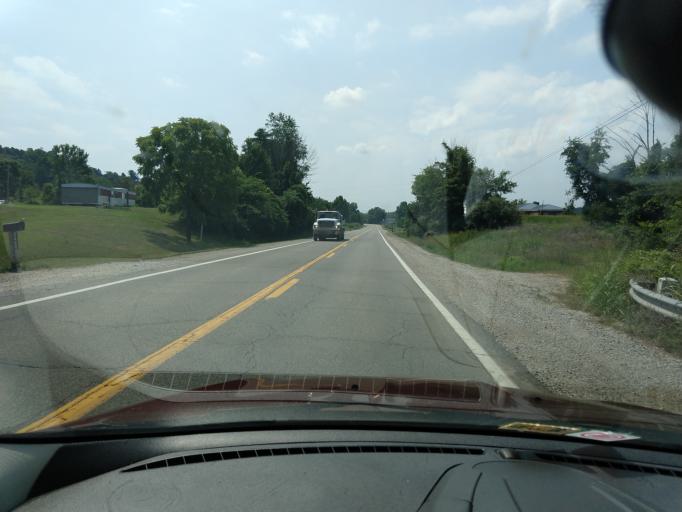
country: US
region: West Virginia
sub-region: Jackson County
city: Ravenswood
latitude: 38.8754
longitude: -81.8269
